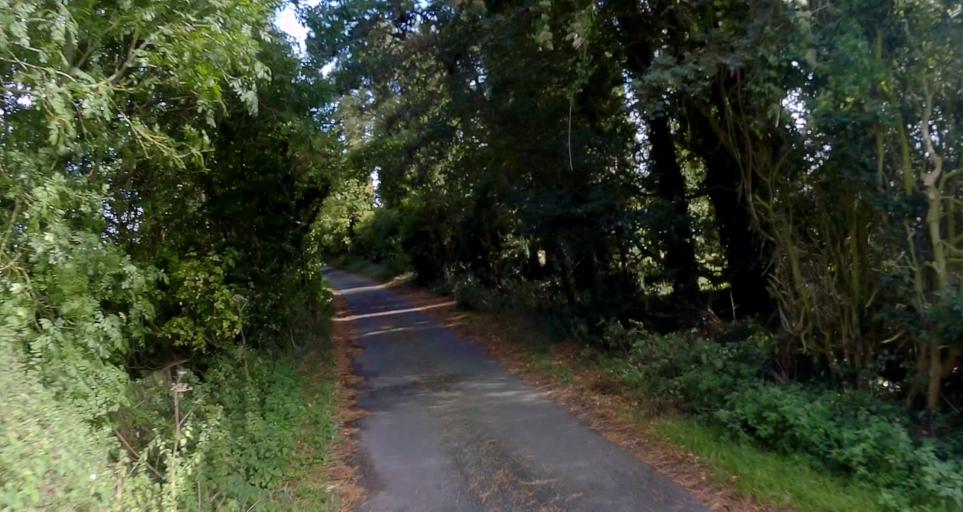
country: GB
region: England
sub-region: Hampshire
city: Kings Worthy
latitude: 51.0827
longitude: -1.2097
